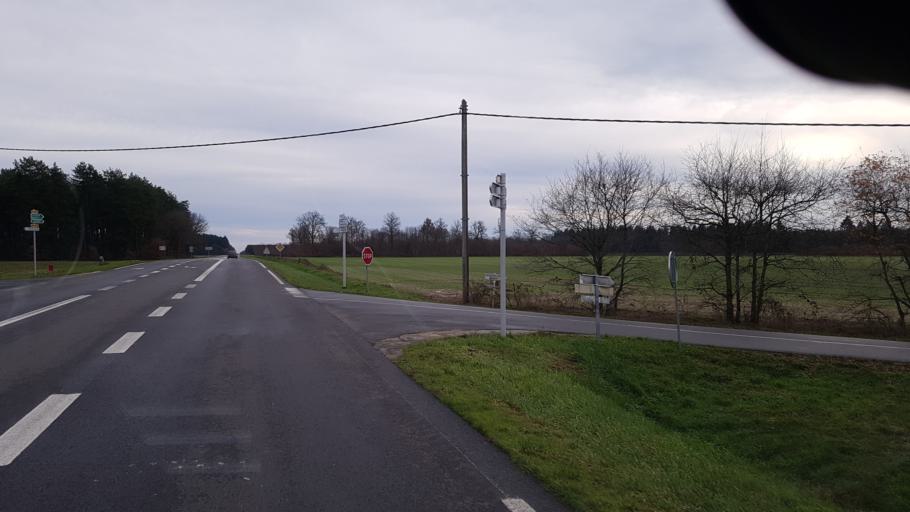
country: FR
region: Centre
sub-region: Departement du Loir-et-Cher
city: Lamotte-Beuvron
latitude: 47.6464
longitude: 1.9924
